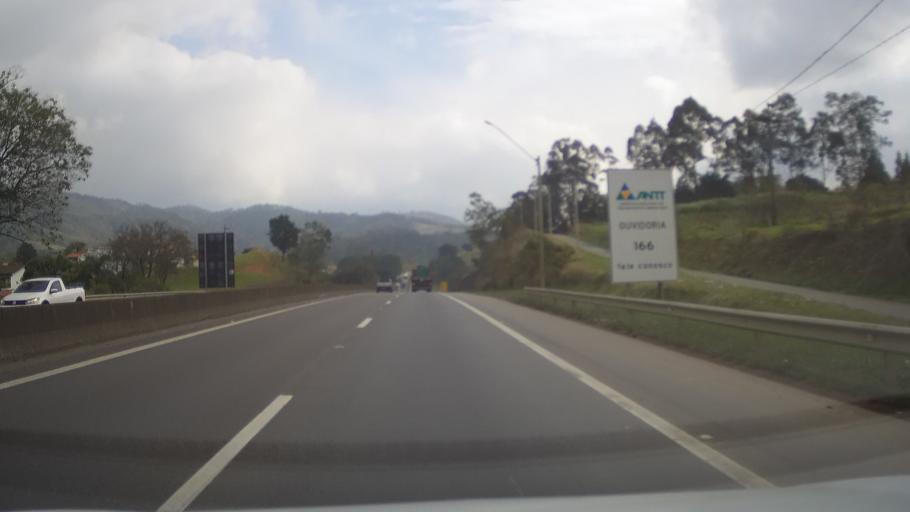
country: BR
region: Minas Gerais
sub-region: Extrema
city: Extrema
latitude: -22.8906
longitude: -46.4132
